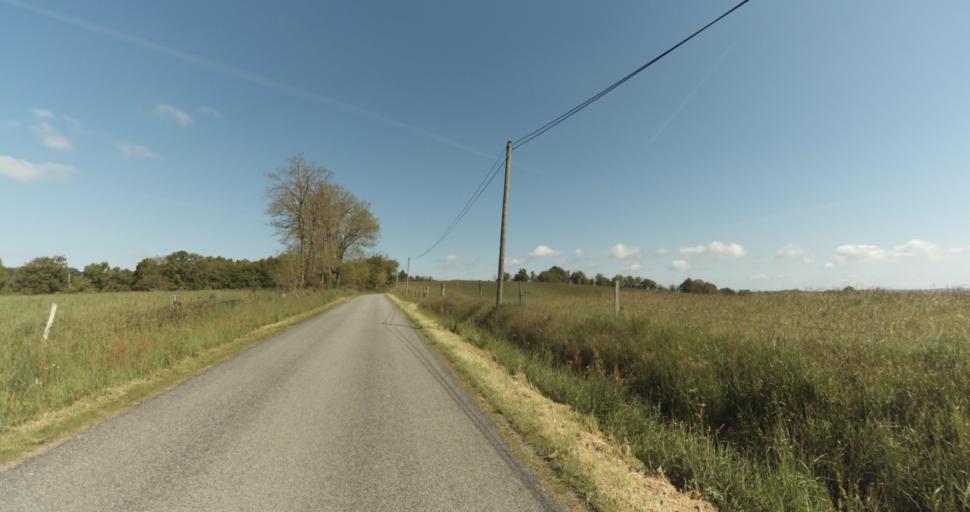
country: FR
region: Limousin
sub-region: Departement de la Haute-Vienne
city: Le Vigen
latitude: 45.7038
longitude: 1.3017
